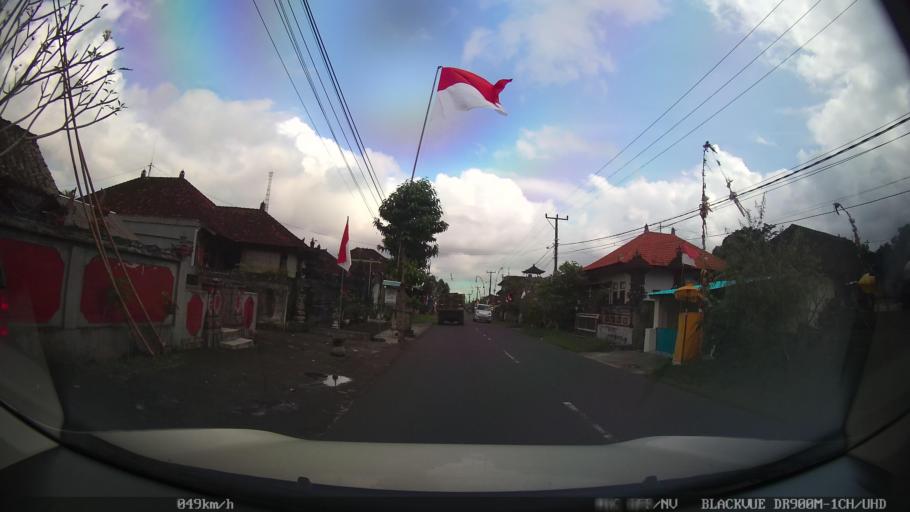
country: ID
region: Bali
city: Rejasa Kaja
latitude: -8.4576
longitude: 115.1385
